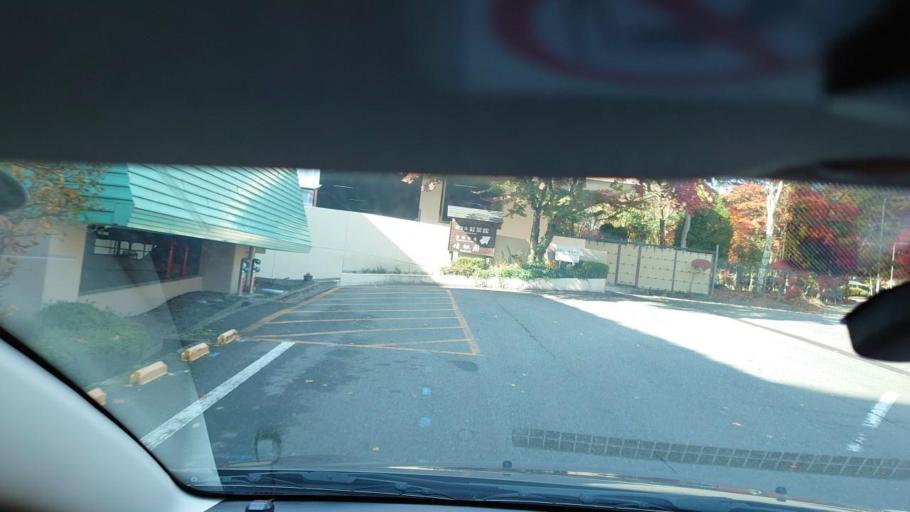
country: JP
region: Iwate
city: Hanamaki
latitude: 39.4524
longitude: 141.0691
